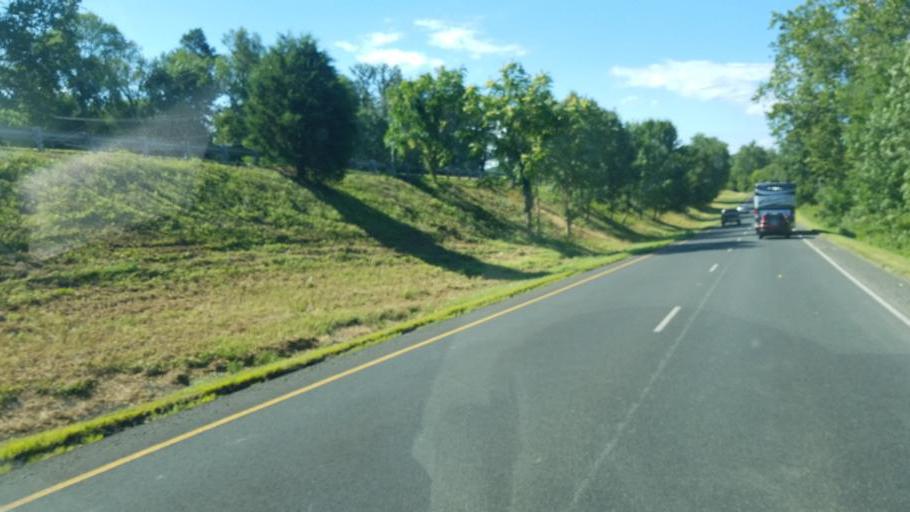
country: US
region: Virginia
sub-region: Fauquier County
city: Warrenton
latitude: 38.7834
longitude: -77.8240
